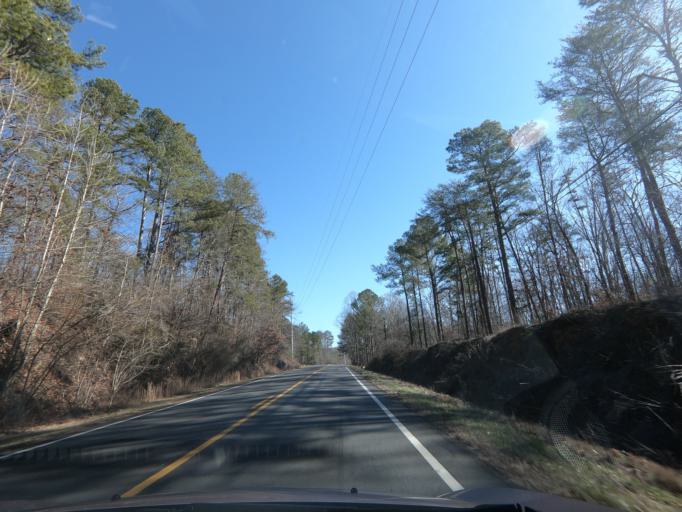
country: US
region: Georgia
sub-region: Dawson County
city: Dawsonville
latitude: 34.3530
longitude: -84.0978
